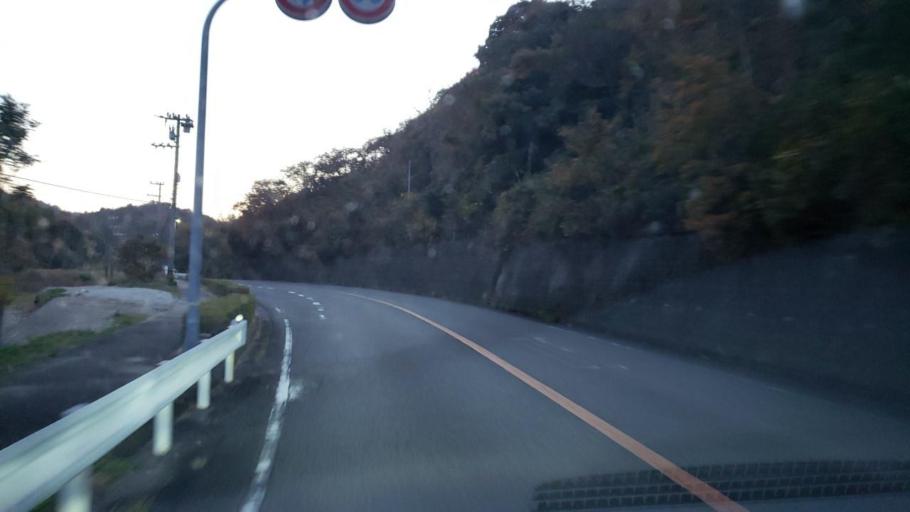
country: JP
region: Hyogo
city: Fukura
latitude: 34.2770
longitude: 134.6781
